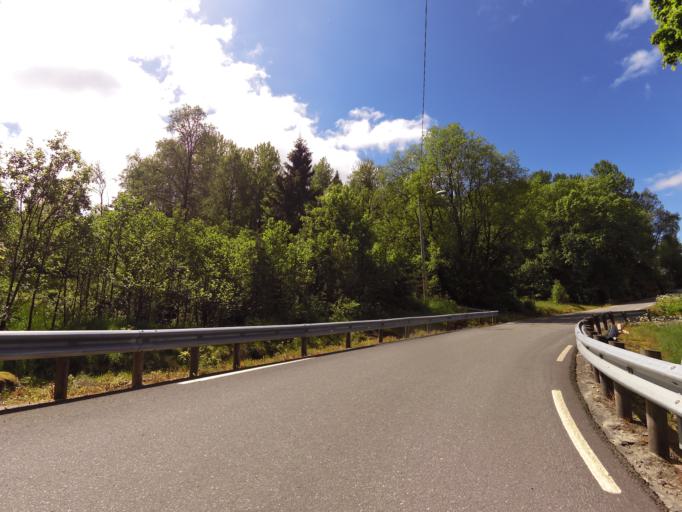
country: NO
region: Vest-Agder
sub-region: Kvinesdal
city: Liknes
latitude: 58.2872
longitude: 6.9393
